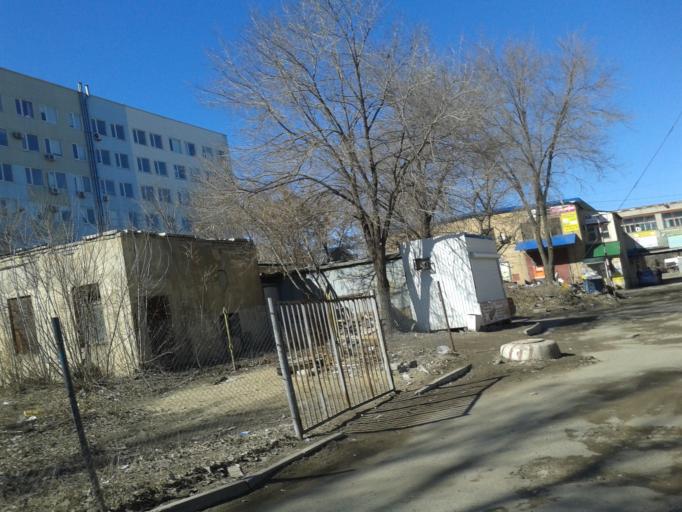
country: RU
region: Volgograd
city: Krasnoslobodsk
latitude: 48.7525
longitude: 44.5477
